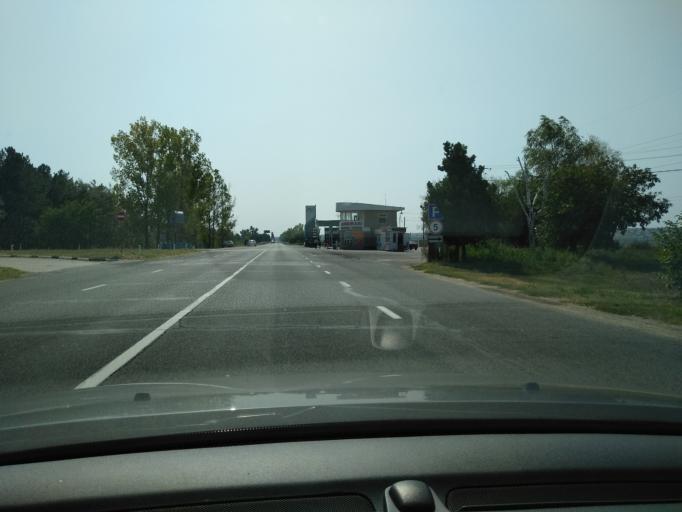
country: RO
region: Vaslui
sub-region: Comuna Dranceni
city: Dranceni
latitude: 46.8513
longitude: 28.2111
